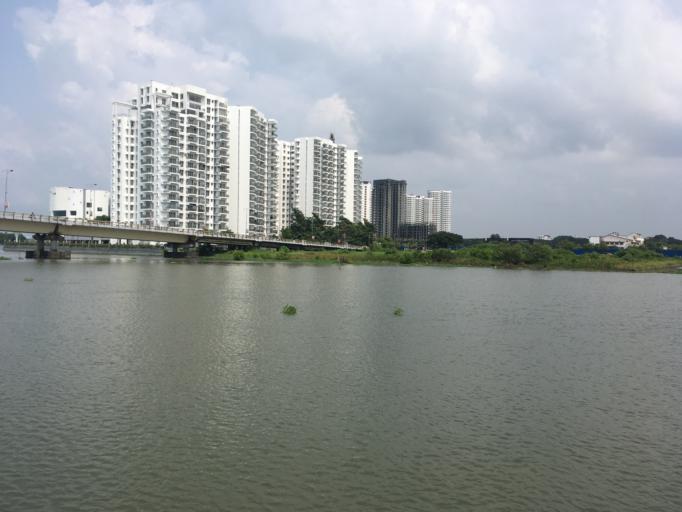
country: IN
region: Kerala
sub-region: Ernakulam
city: Cochin
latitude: 9.9912
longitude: 76.2681
